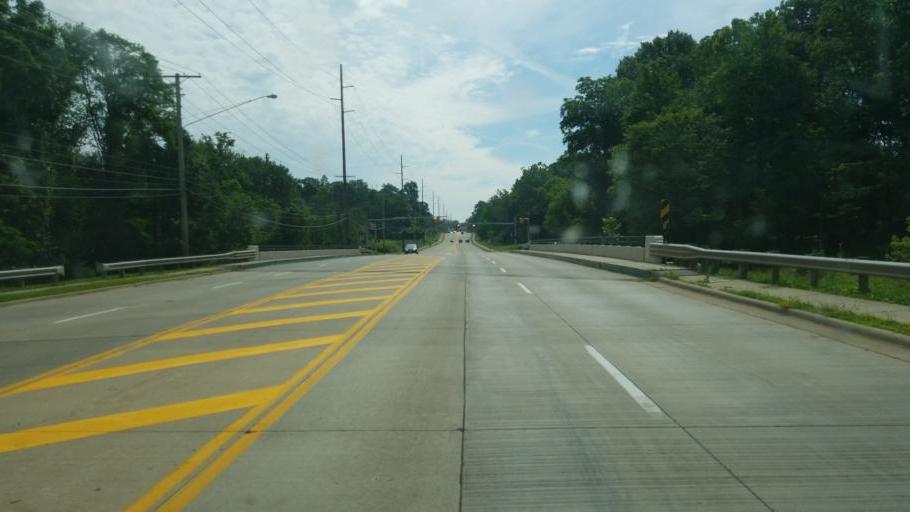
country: US
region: Ohio
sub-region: Cuyahoga County
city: Strongsville
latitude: 41.3132
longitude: -81.7981
